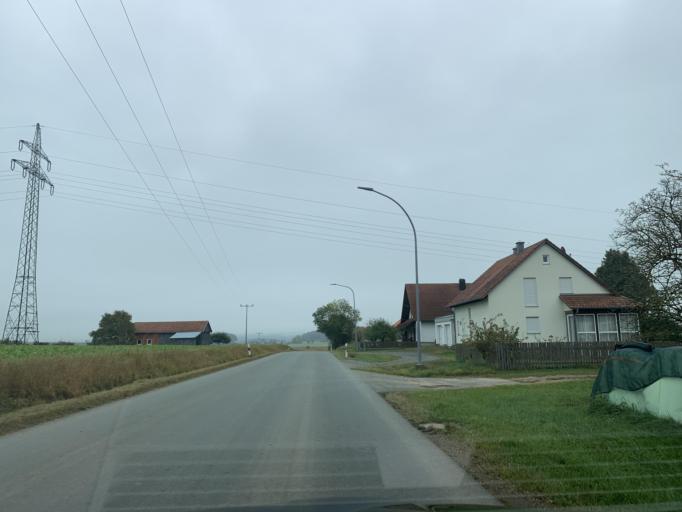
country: DE
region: Bavaria
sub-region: Upper Palatinate
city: Winklarn
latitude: 49.4073
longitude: 12.4678
